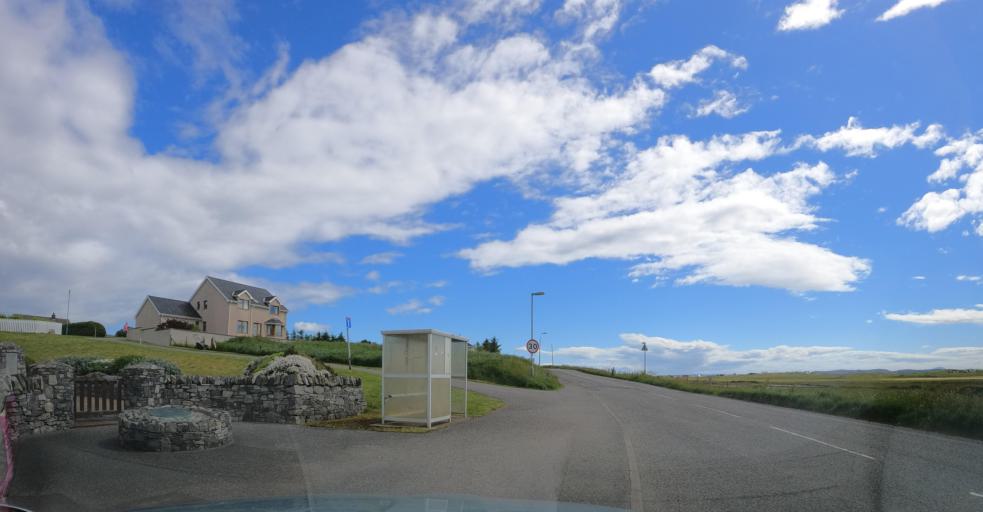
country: GB
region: Scotland
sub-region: Eilean Siar
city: Stornoway
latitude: 58.2093
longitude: -6.3231
